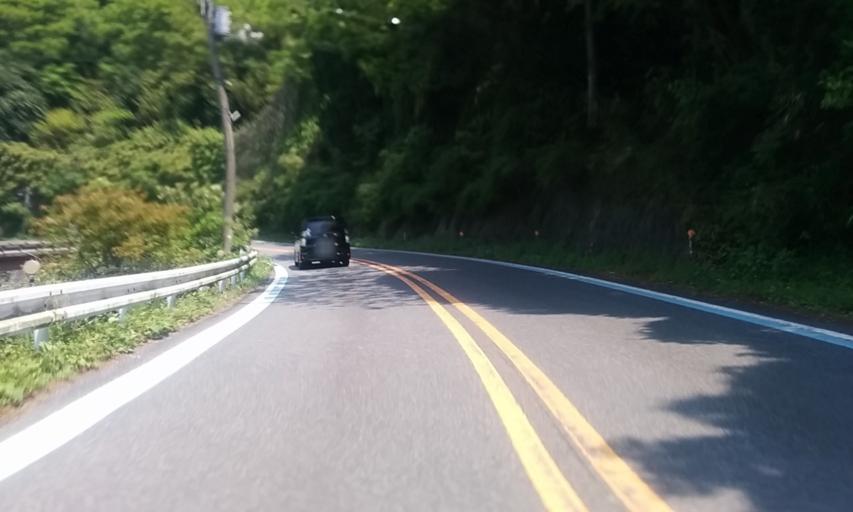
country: JP
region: Ehime
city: Niihama
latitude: 33.9191
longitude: 133.3117
